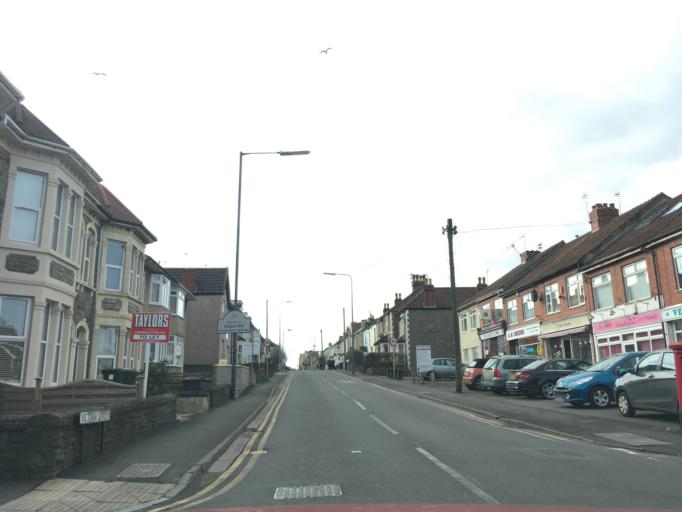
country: GB
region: England
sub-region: South Gloucestershire
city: Mangotsfield
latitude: 51.4832
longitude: -2.5064
